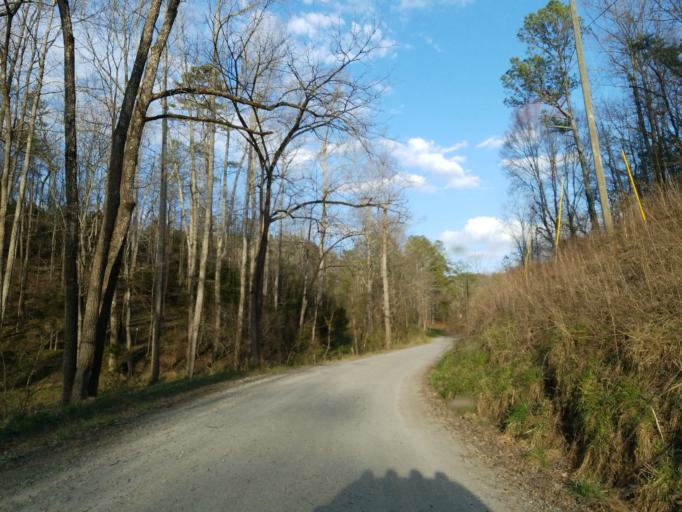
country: US
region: Georgia
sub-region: Bartow County
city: Rydal
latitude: 34.5030
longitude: -84.6398
